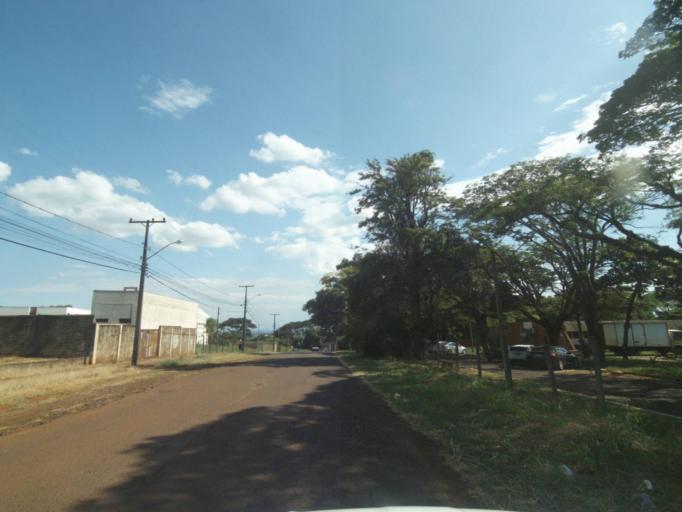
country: BR
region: Parana
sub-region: Londrina
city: Londrina
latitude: -23.3271
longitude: -51.1940
